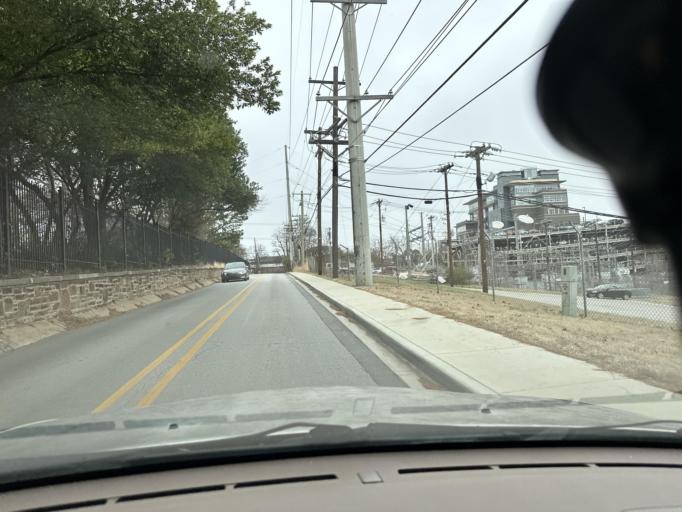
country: US
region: Arkansas
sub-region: Washington County
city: Fayetteville
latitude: 36.0645
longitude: -94.1682
